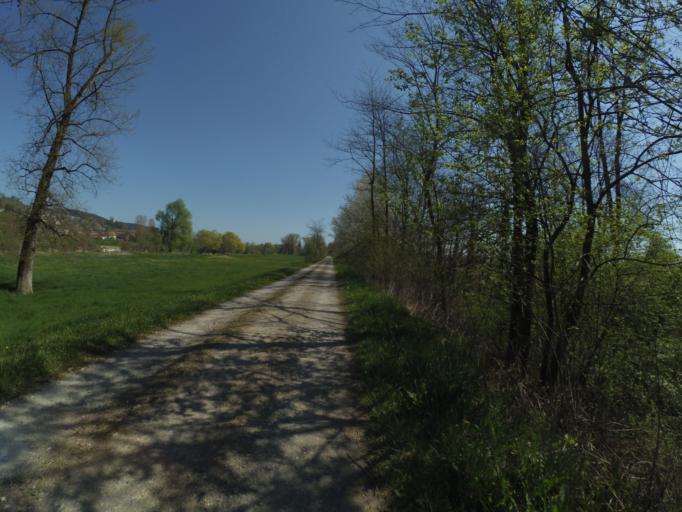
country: CH
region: Thurgau
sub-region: Frauenfeld District
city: Gachnang
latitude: 47.5787
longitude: 8.8221
